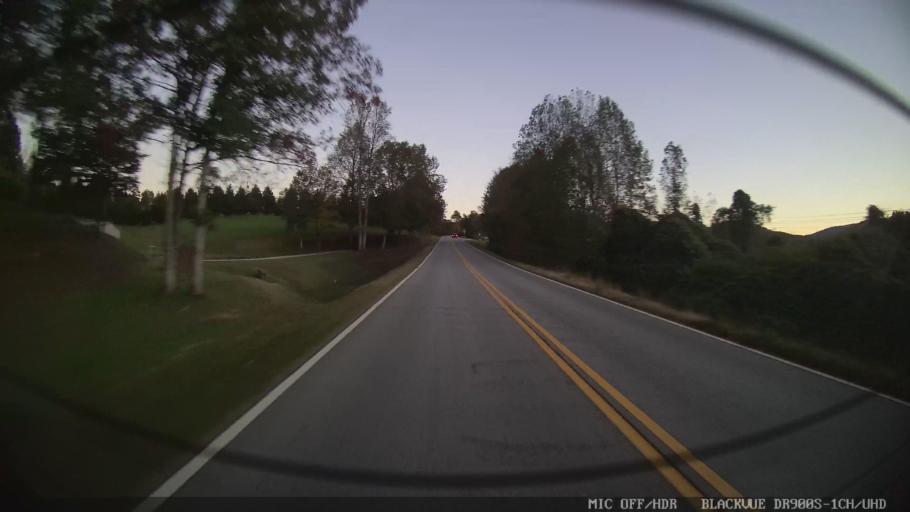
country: US
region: North Carolina
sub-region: Clay County
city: Hayesville
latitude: 34.9588
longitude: -83.8698
